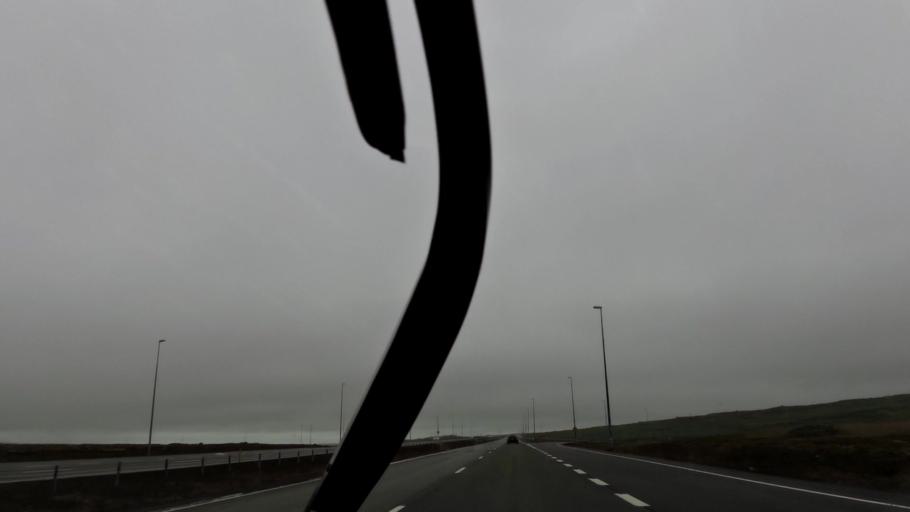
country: IS
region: Southern Peninsula
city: Vogar
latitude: 63.9631
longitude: -22.4158
